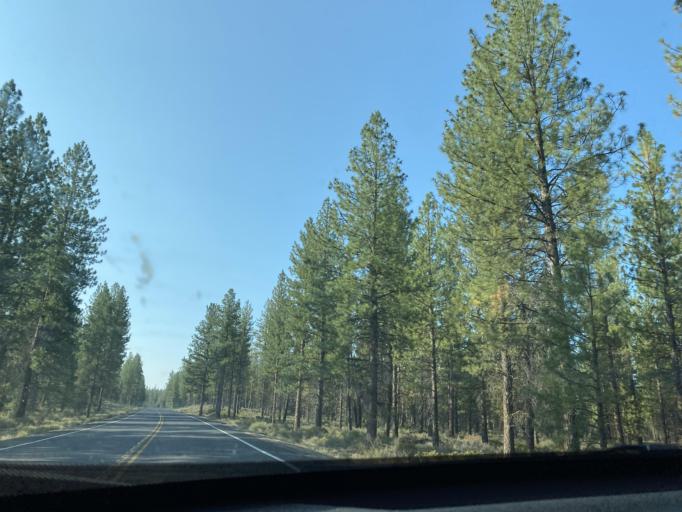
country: US
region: Oregon
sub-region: Deschutes County
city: La Pine
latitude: 43.7184
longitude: -121.4140
